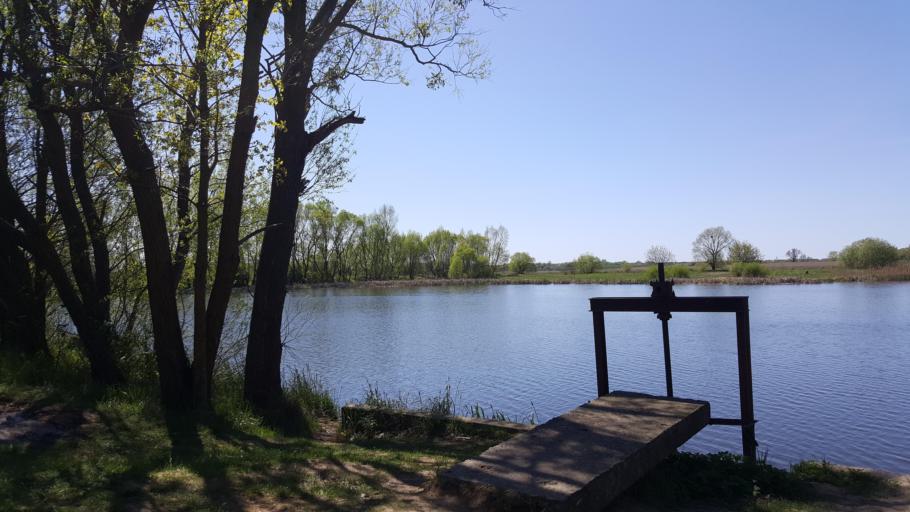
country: BY
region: Brest
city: Kamyanyets
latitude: 52.4349
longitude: 23.8521
